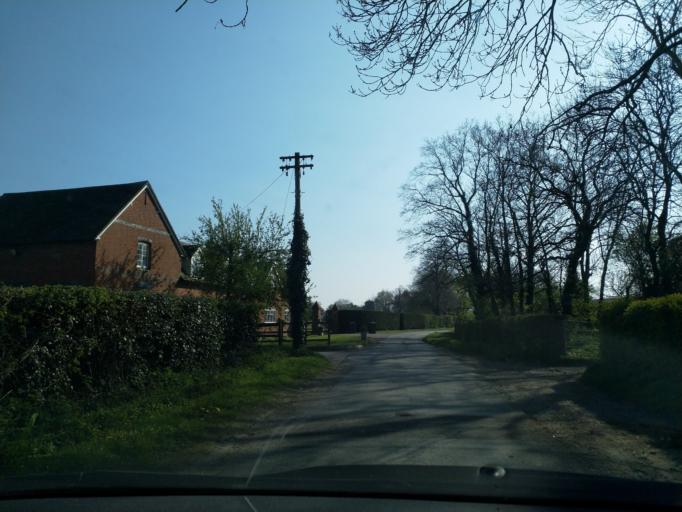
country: GB
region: England
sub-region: Warwickshire
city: Wroxall
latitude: 52.2882
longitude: -1.6959
